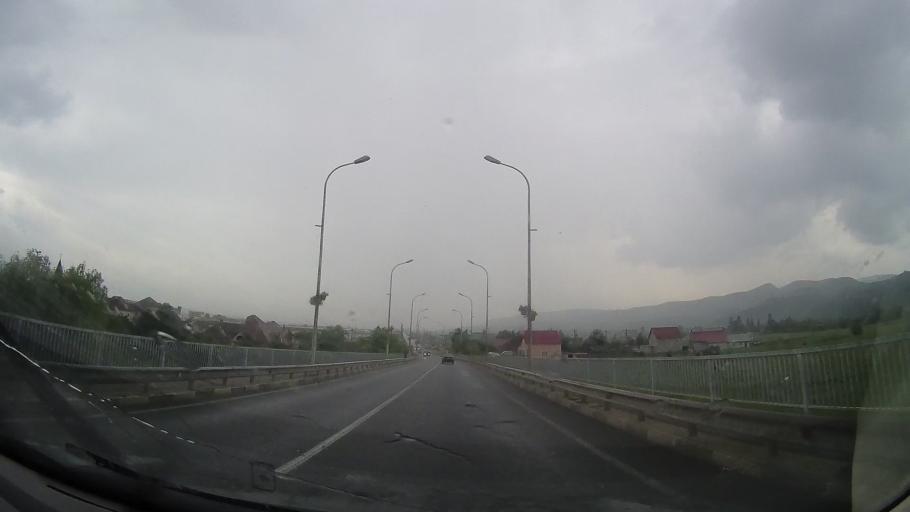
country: RO
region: Caras-Severin
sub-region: Comuna Buchin
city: Buchin
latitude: 45.3839
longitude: 22.2310
